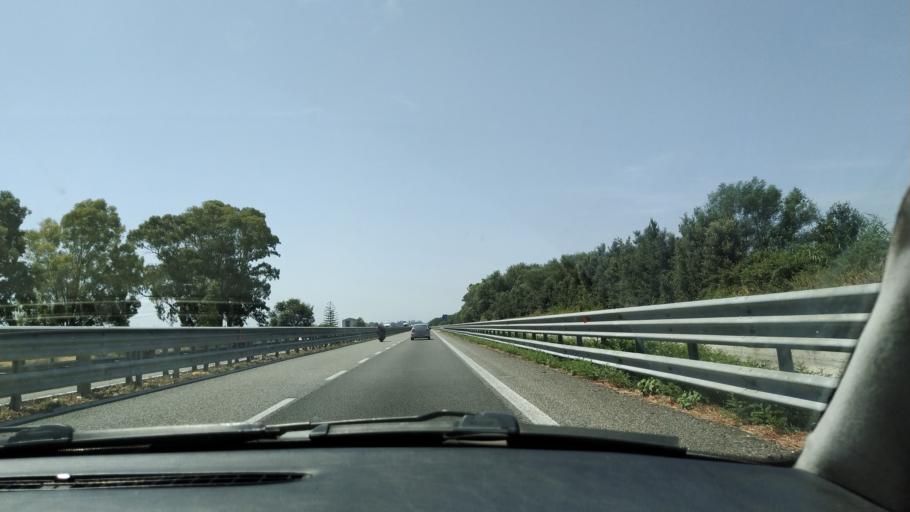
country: IT
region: Basilicate
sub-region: Provincia di Matera
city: Marconia
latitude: 40.3535
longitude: 16.7724
